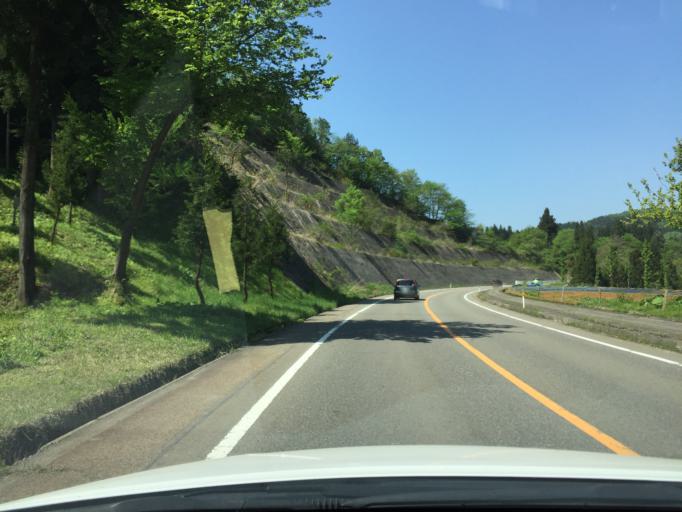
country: JP
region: Niigata
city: Kamo
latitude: 37.6337
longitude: 139.1039
